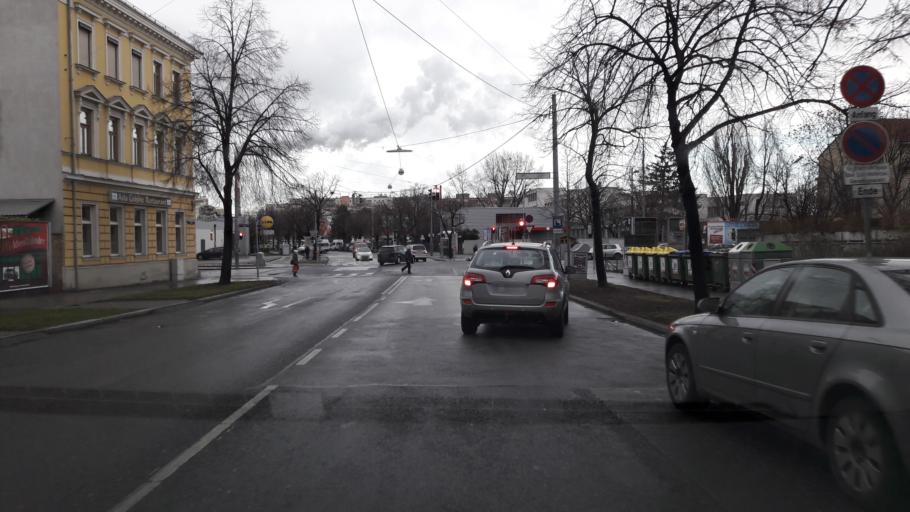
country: AT
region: Lower Austria
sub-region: Politischer Bezirk Wien-Umgebung
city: Schwechat
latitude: 48.1651
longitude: 16.4310
